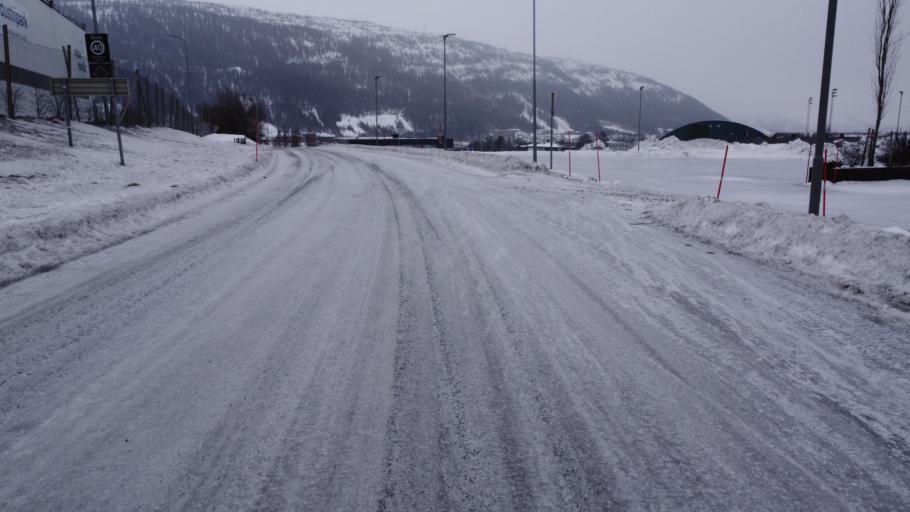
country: NO
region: Nordland
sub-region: Rana
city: Mo i Rana
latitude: 66.3127
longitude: 14.1583
